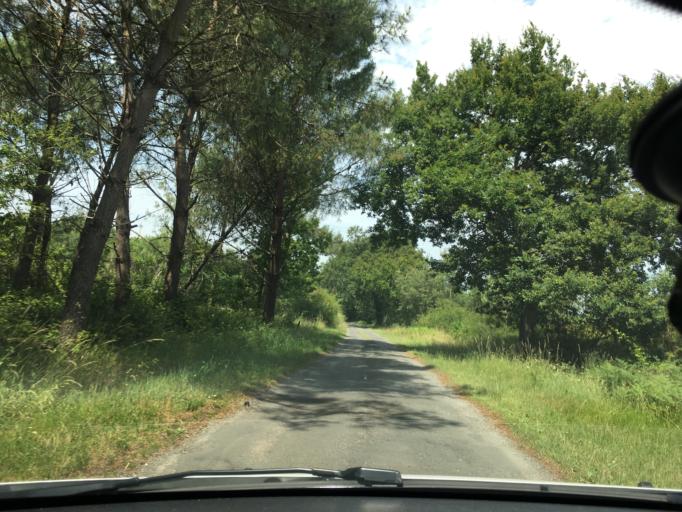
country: FR
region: Aquitaine
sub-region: Departement de la Gironde
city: Lesparre-Medoc
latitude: 45.2797
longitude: -0.9069
